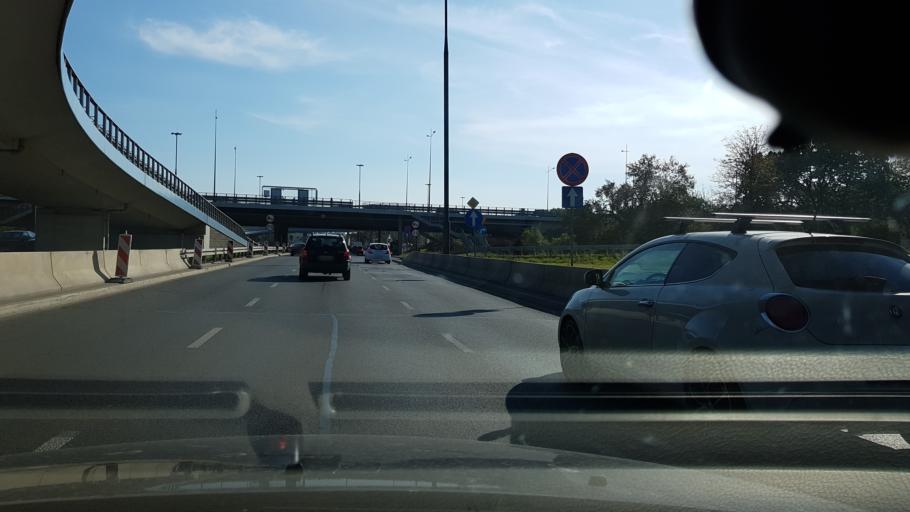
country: PL
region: Masovian Voivodeship
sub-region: Warszawa
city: Srodmiescie
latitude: 52.2253
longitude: 21.0432
